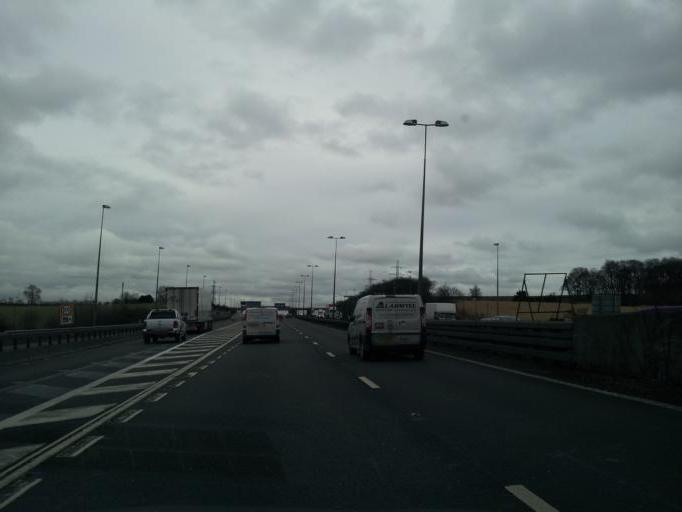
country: GB
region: England
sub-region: Staffordshire
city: Featherstone
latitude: 52.6737
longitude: -2.0814
